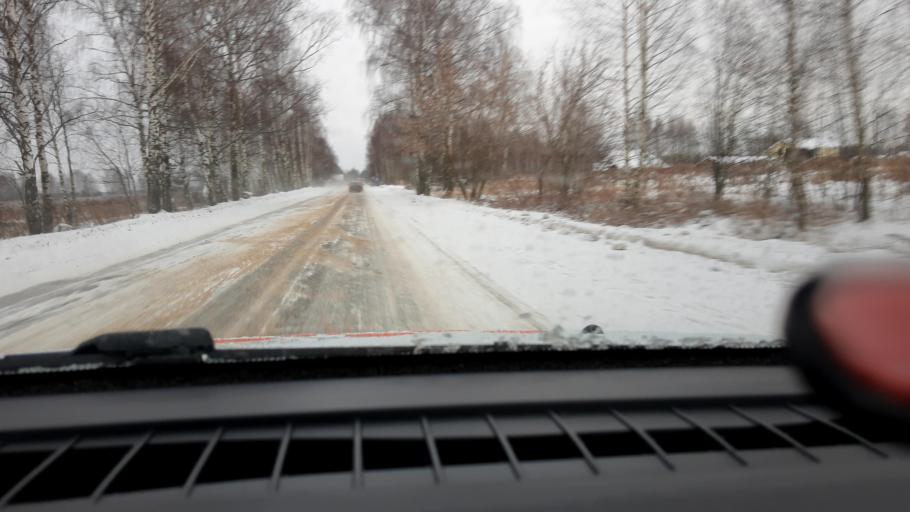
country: RU
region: Nizjnij Novgorod
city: Pamyat' Parizhskoy Kommuny
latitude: 56.2676
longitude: 44.4290
